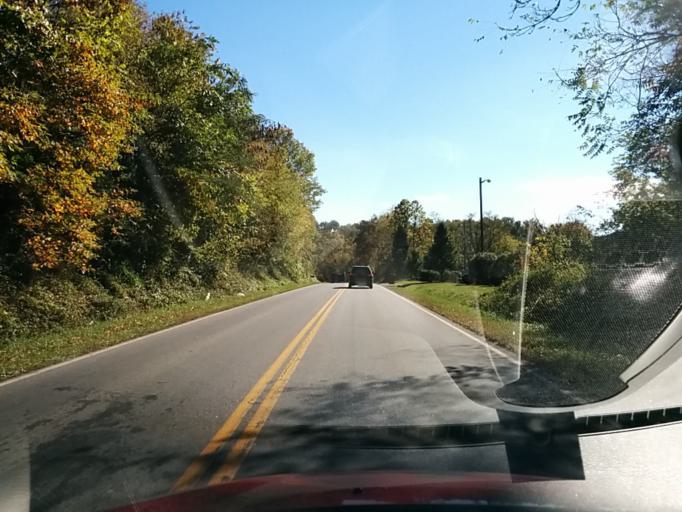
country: US
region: Virginia
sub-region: Roanoke County
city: Hollins
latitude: 37.3546
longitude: -79.9283
